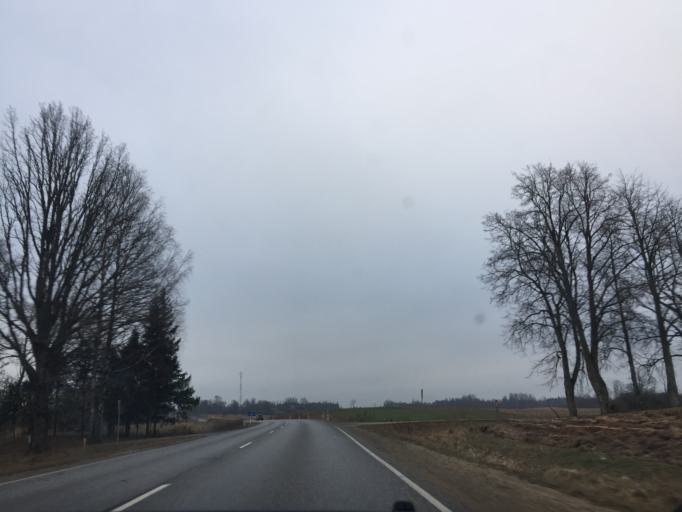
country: LV
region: Raunas
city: Rauna
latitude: 57.2866
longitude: 25.4904
